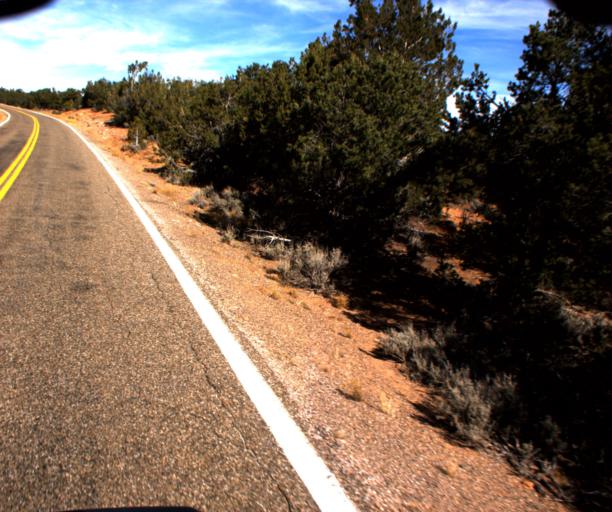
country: US
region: Arizona
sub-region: Navajo County
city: Kayenta
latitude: 36.6376
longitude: -110.5104
